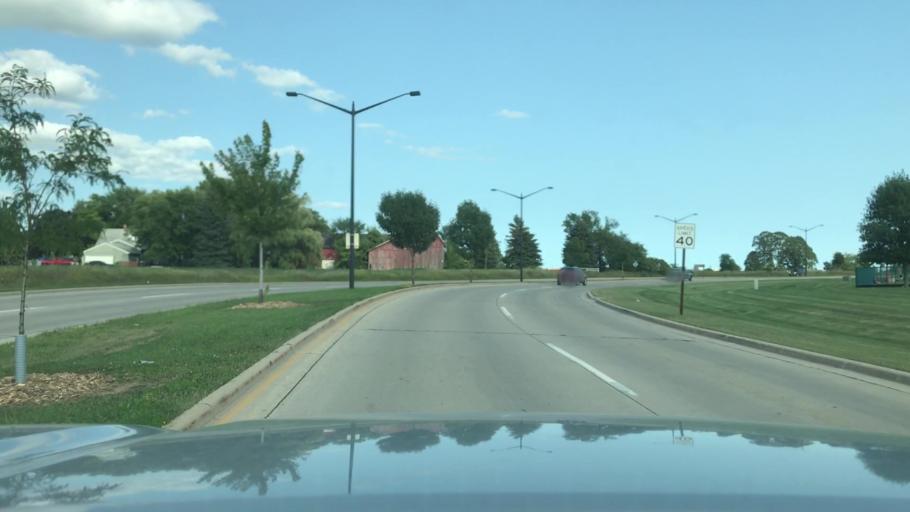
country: US
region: Wisconsin
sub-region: Brown County
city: Bellevue
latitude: 44.4872
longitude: -87.9269
